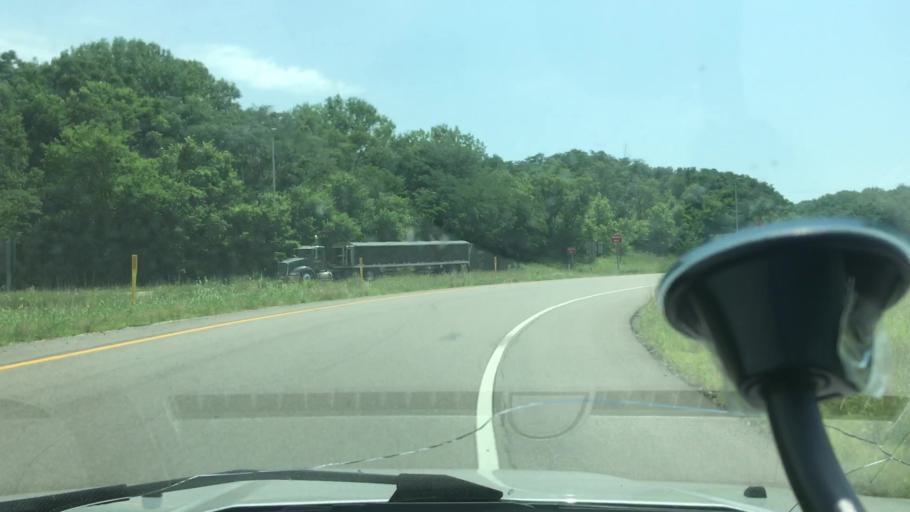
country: US
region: Illinois
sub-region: Tazewell County
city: Marquette Heights
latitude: 40.6313
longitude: -89.6111
